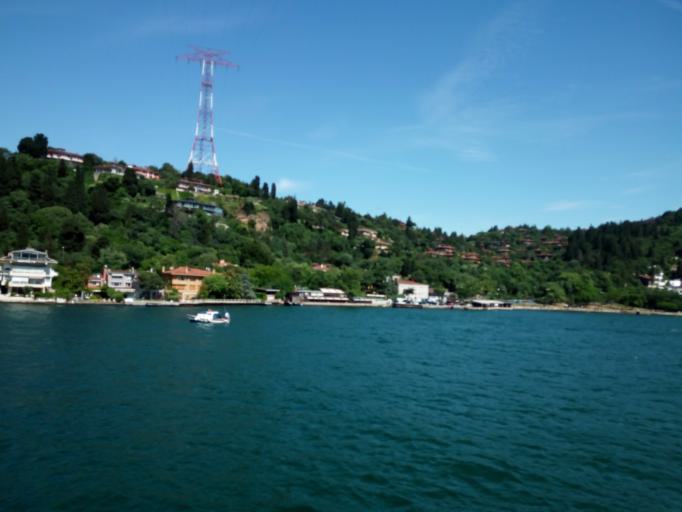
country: TR
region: Istanbul
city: UEskuedar
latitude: 41.0708
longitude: 29.0541
